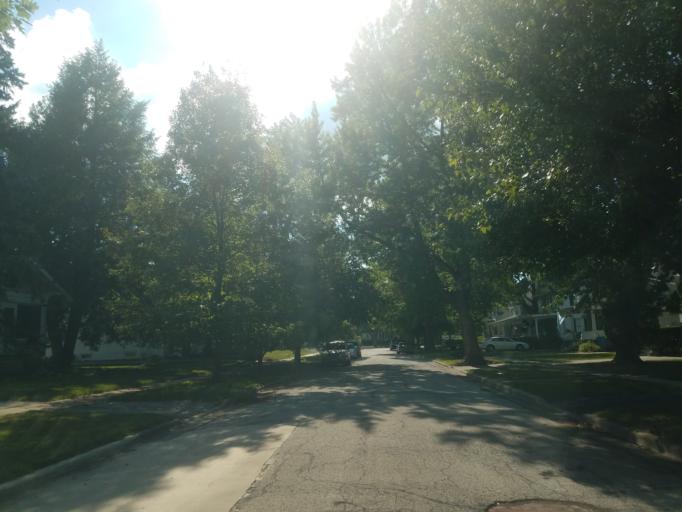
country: US
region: Illinois
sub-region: McLean County
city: Bloomington
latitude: 40.4764
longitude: -88.9662
